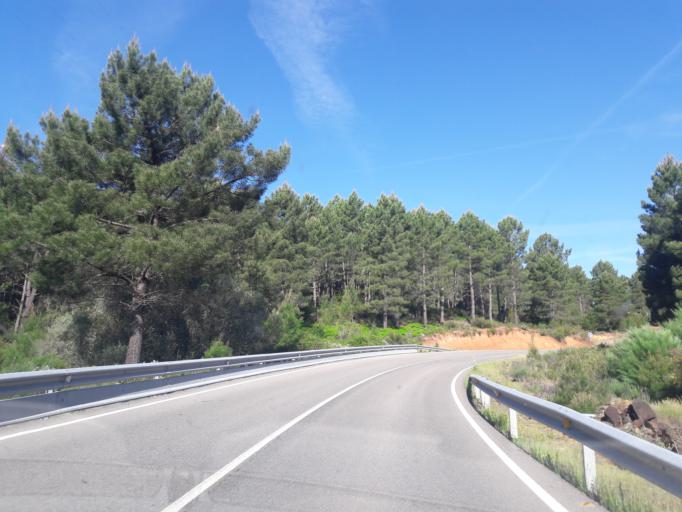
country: ES
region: Castille and Leon
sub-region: Provincia de Salamanca
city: Herguijuela de la Sierra
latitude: 40.4118
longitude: -6.1001
